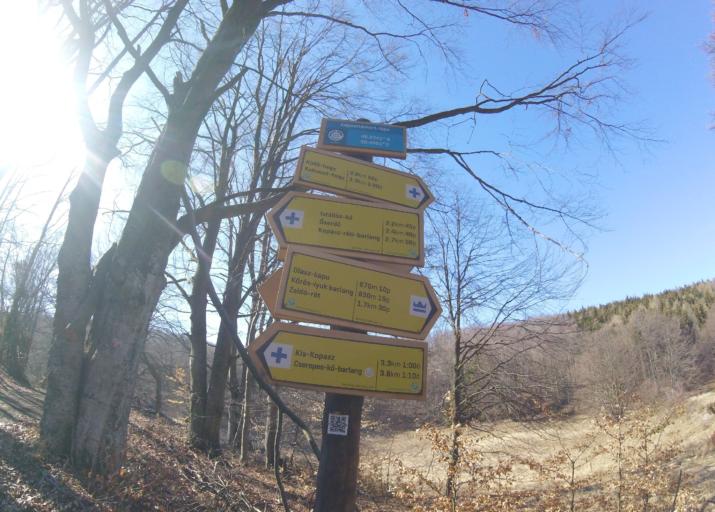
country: HU
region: Heves
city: Szilvasvarad
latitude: 48.0742
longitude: 20.4462
